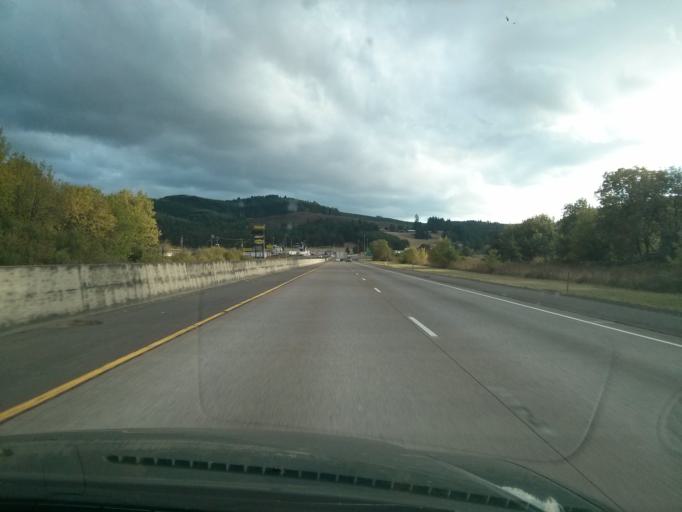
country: US
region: Oregon
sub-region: Douglas County
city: Yoncalla
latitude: 43.5431
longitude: -123.2895
